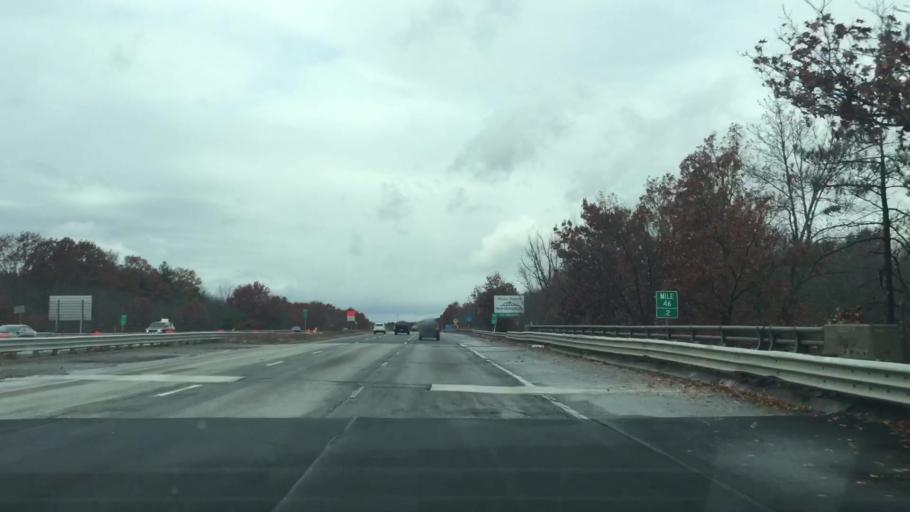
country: US
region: Massachusetts
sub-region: Essex County
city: Methuen
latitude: 42.7428
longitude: -71.2090
